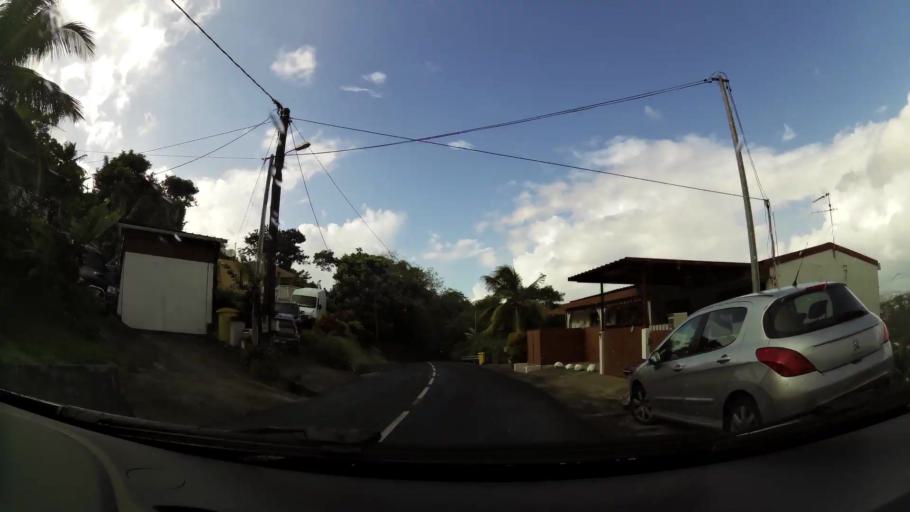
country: MQ
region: Martinique
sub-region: Martinique
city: Saint-Esprit
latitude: 14.5100
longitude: -60.9625
